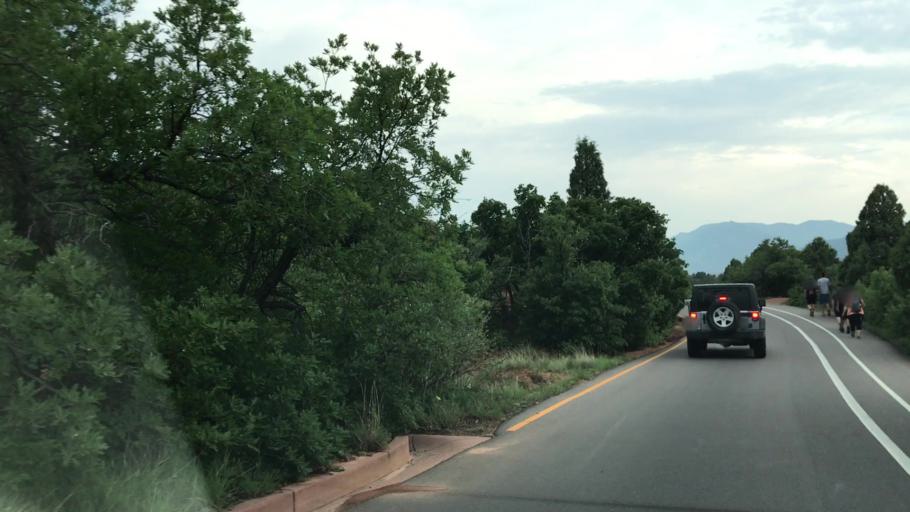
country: US
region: Colorado
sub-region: El Paso County
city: Manitou Springs
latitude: 38.8705
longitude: -104.8809
